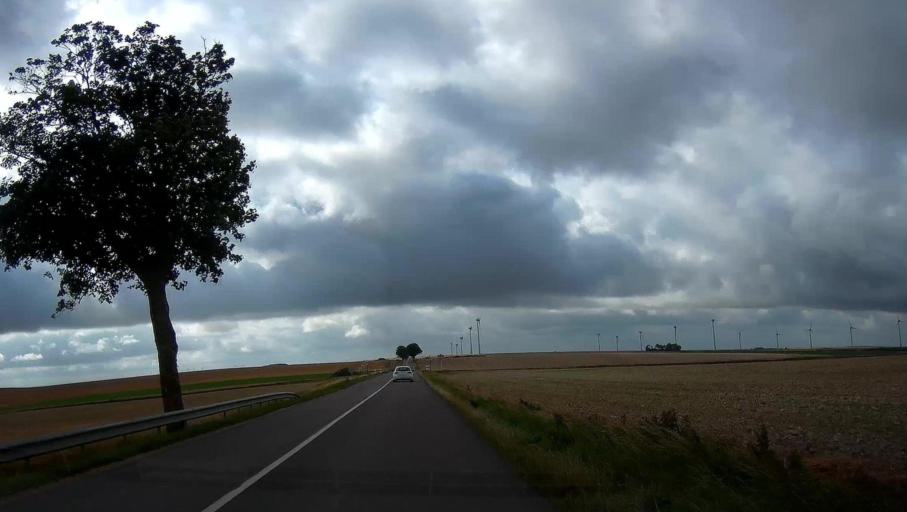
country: FR
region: Champagne-Ardenne
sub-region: Departement des Ardennes
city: Chateau-Porcien
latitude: 49.5811
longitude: 4.2511
